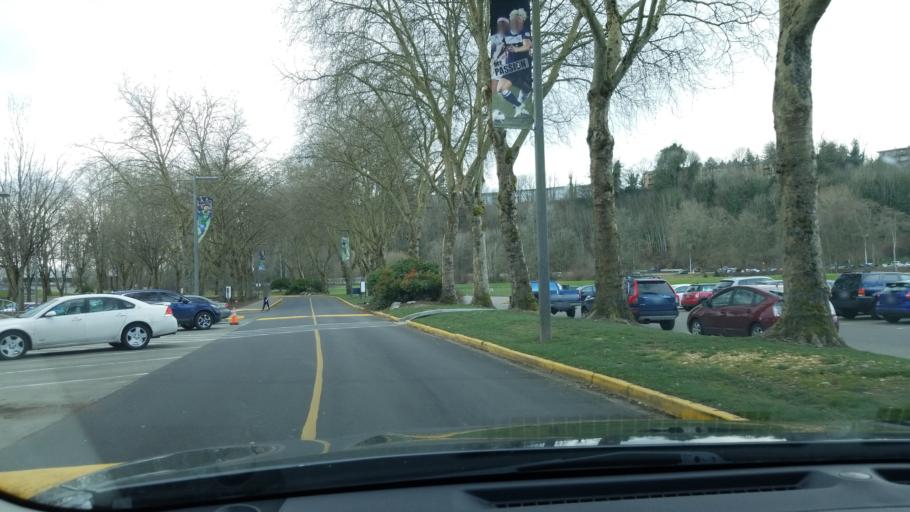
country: US
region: Washington
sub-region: King County
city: Tukwila
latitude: 47.4700
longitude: -122.2502
